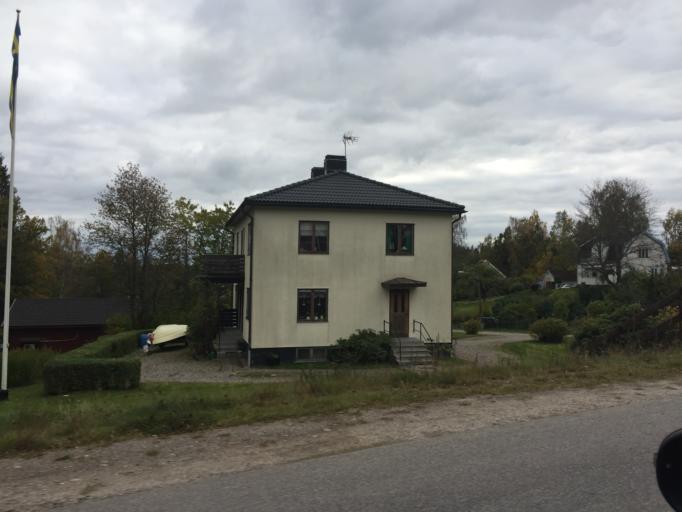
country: SE
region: OEstergoetland
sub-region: Linkopings Kommun
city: Ljungsbro
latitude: 58.7901
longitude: 15.4910
